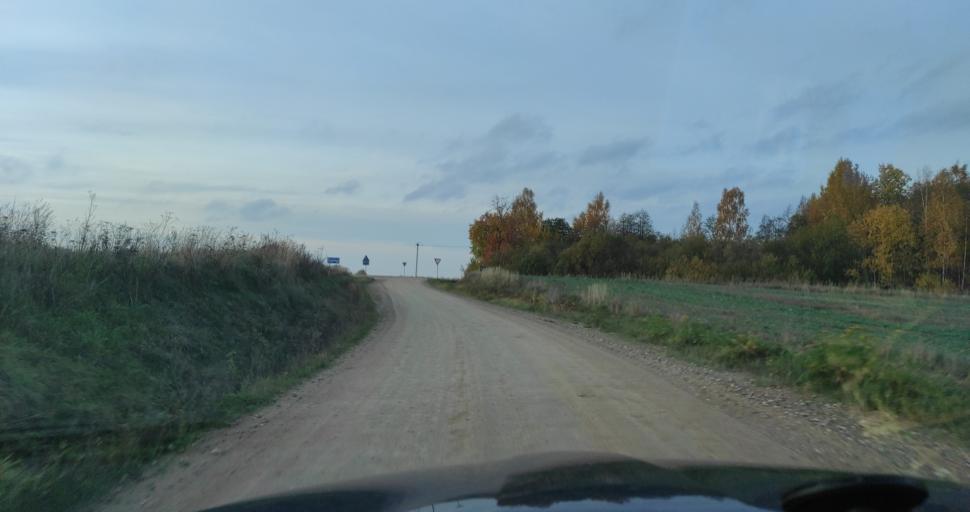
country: LV
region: Skrunda
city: Skrunda
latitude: 56.6390
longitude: 21.8100
